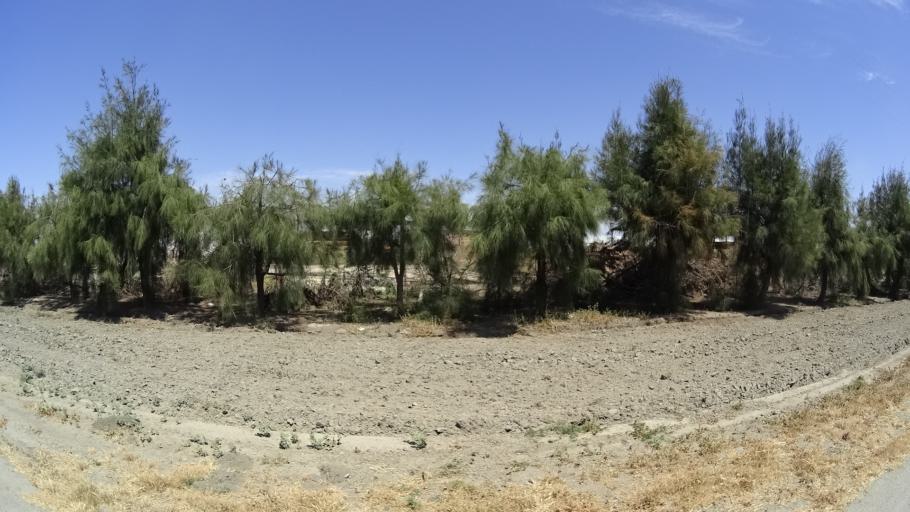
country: US
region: California
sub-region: Kings County
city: Stratford
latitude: 36.1525
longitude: -119.7428
